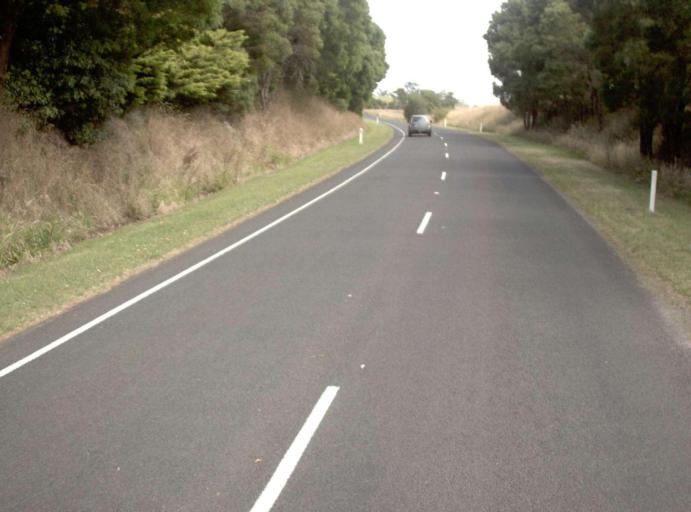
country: AU
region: Victoria
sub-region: Cardinia
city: Bunyip
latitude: -38.3409
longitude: 145.7365
